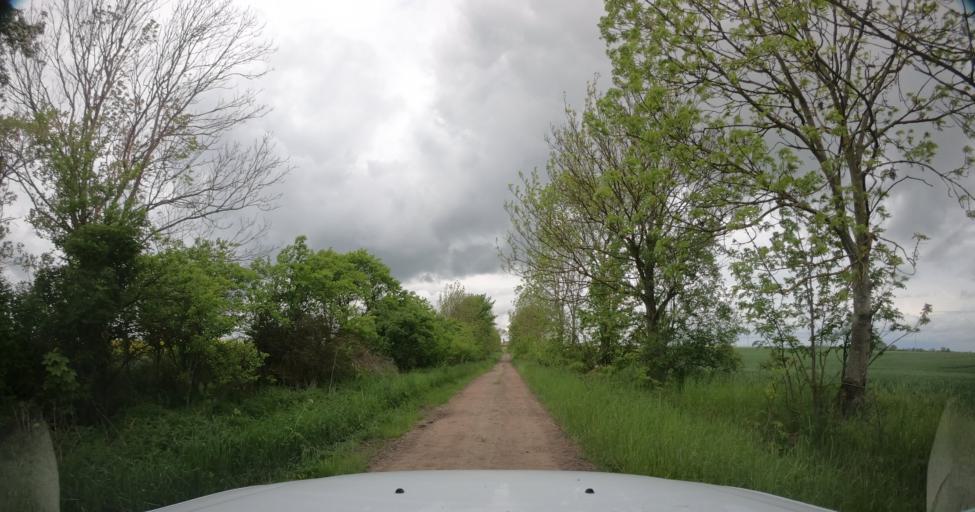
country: PL
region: West Pomeranian Voivodeship
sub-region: Powiat pyrzycki
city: Kozielice
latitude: 53.0913
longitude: 14.8173
